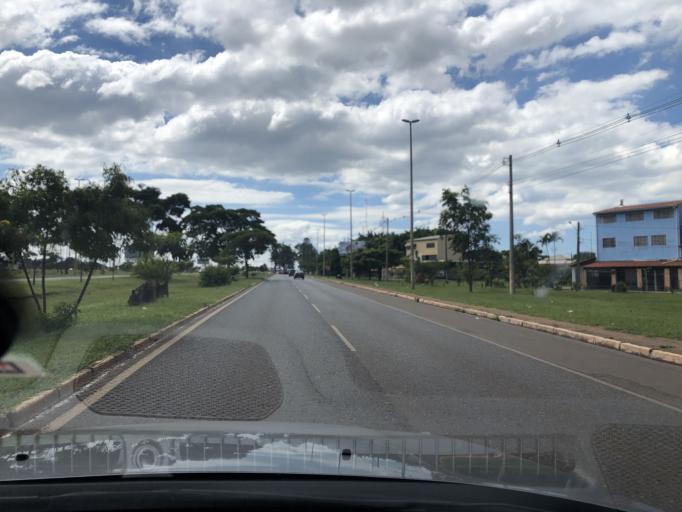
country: BR
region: Federal District
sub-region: Brasilia
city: Brasilia
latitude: -15.9966
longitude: -48.0563
